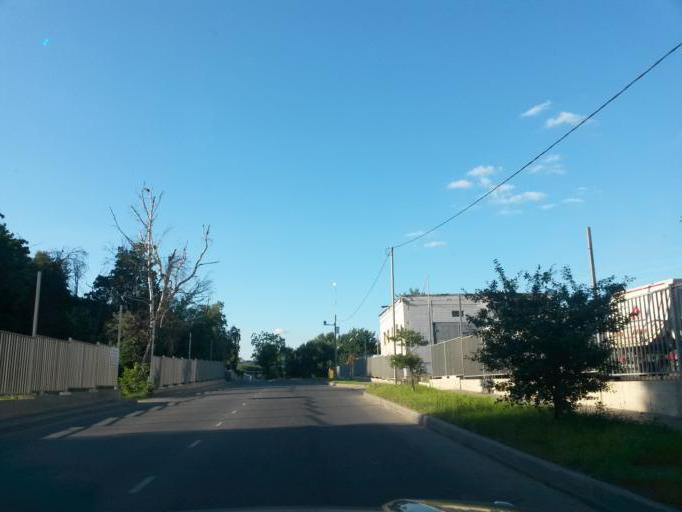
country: RU
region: Moscow
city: Annino
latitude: 55.5769
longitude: 37.6079
